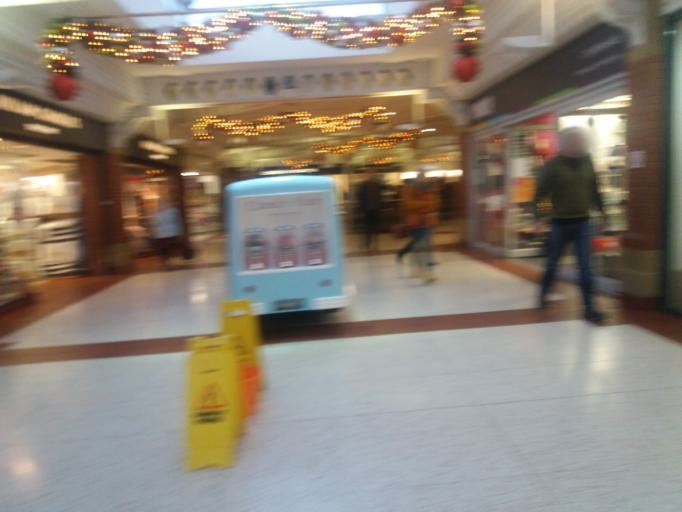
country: GB
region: England
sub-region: Wiltshire
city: Chippenham
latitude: 51.4593
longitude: -2.1150
